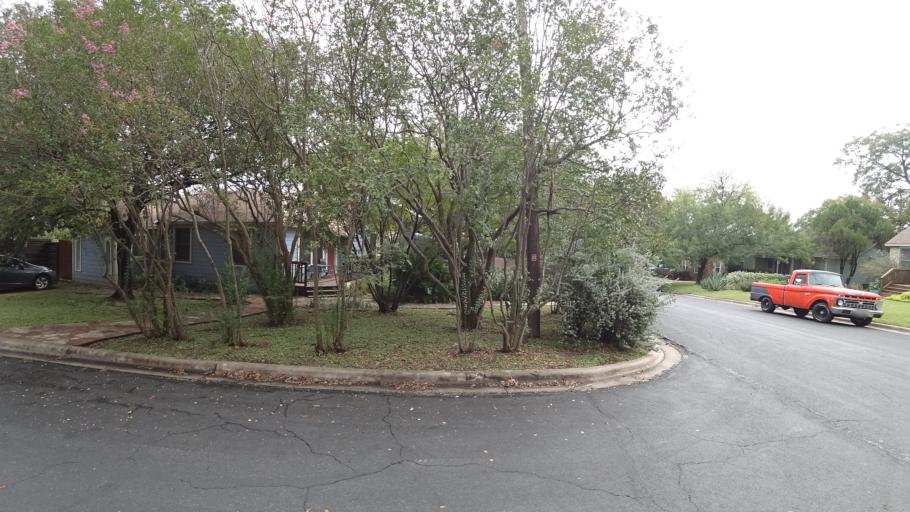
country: US
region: Texas
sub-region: Travis County
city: Rollingwood
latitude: 30.2468
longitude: -97.7794
